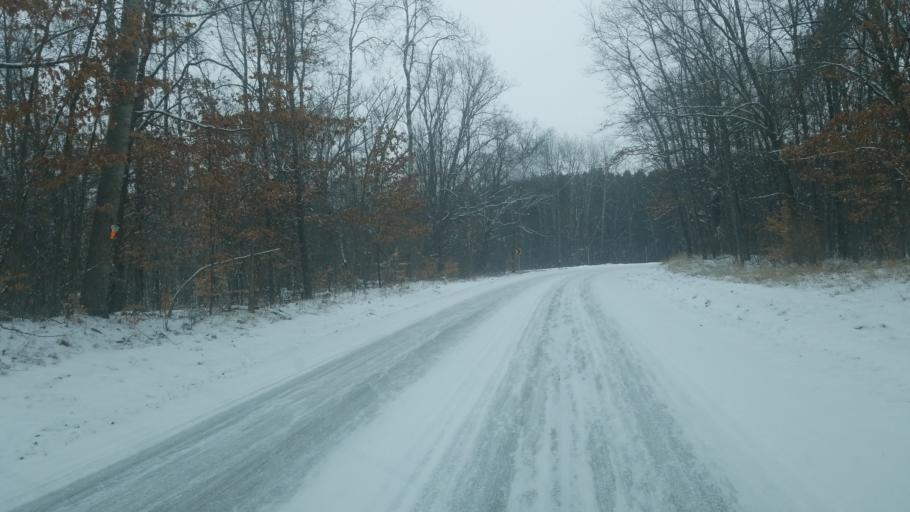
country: US
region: Michigan
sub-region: Mecosta County
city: Big Rapids
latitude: 43.7338
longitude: -85.4120
